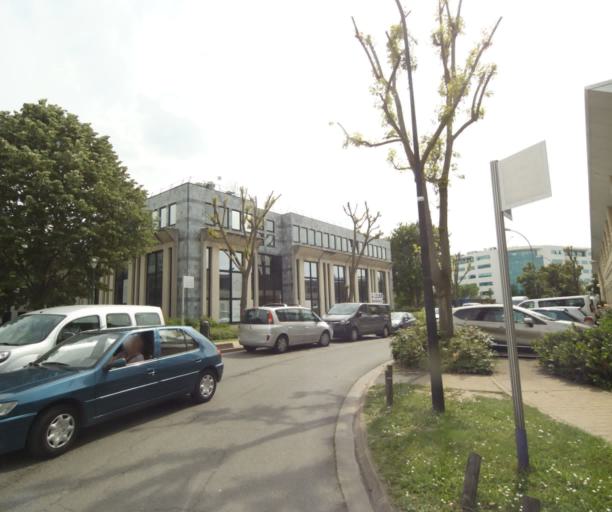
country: FR
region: Ile-de-France
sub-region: Departement des Hauts-de-Seine
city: Gennevilliers
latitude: 48.9350
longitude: 2.3055
